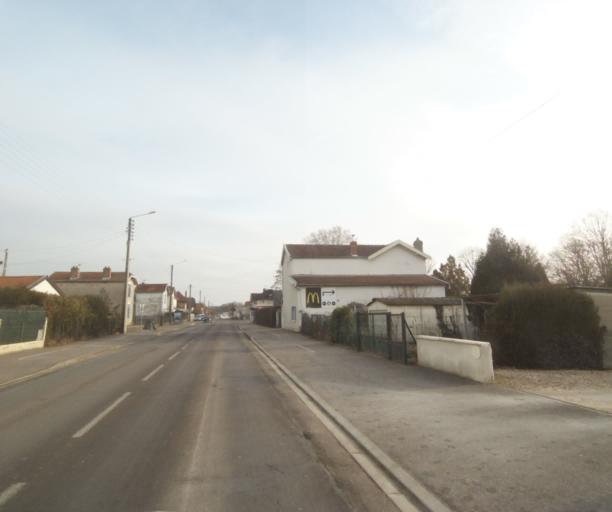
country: FR
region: Champagne-Ardenne
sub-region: Departement de la Haute-Marne
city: Saint-Dizier
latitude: 48.6274
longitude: 4.9498
